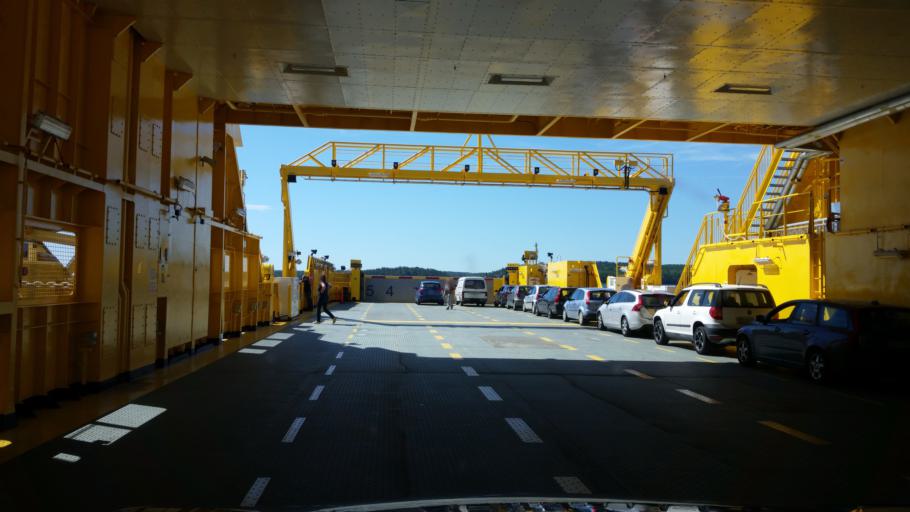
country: FI
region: Varsinais-Suomi
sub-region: Aboland-Turunmaa
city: Laensi-Turunmaa
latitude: 60.2349
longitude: 22.1122
